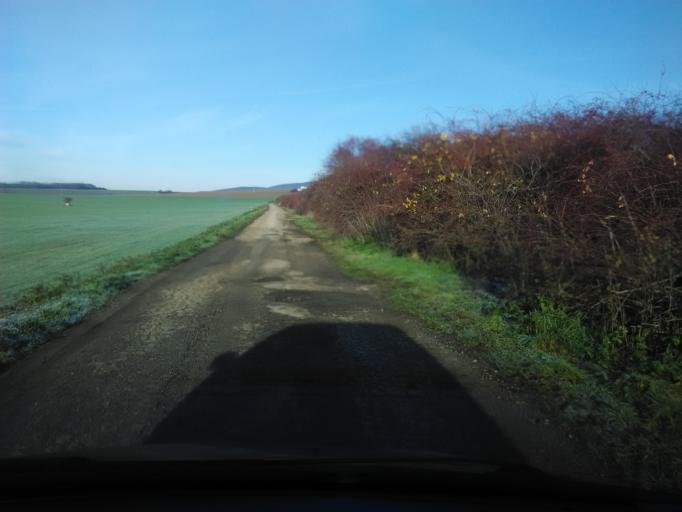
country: SK
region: Nitriansky
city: Tlmace
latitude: 48.3325
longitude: 18.5355
